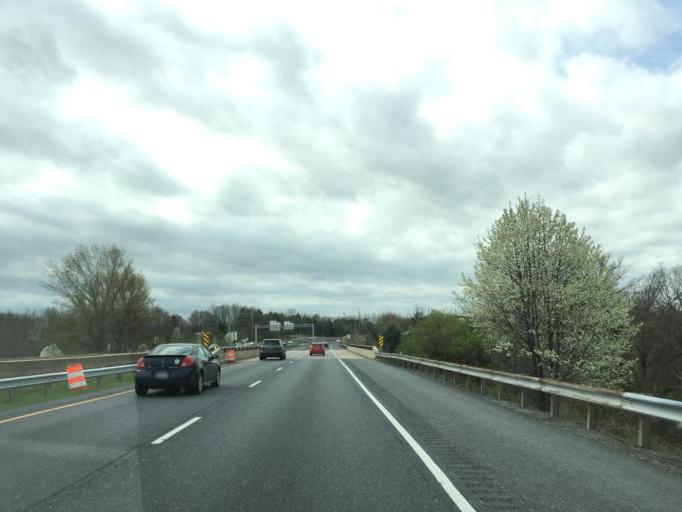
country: US
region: Maryland
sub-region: Frederick County
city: Clover Hill
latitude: 39.4442
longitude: -77.4033
